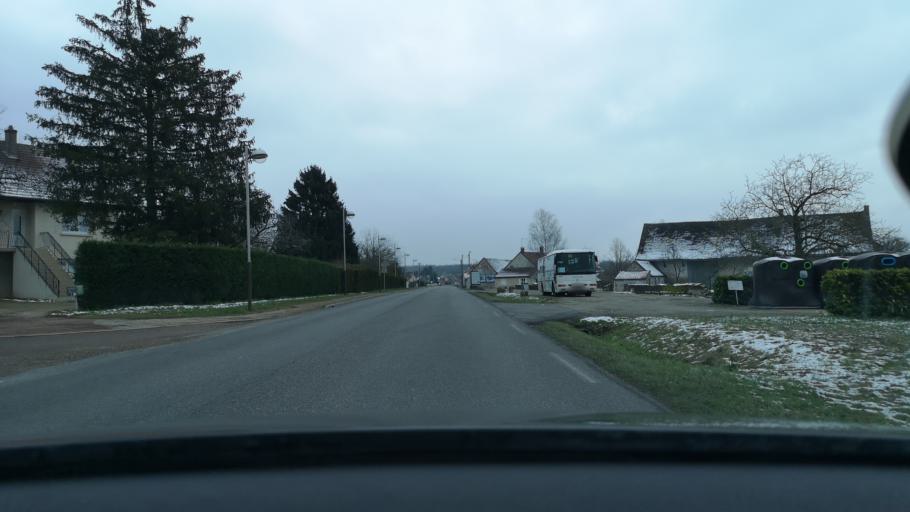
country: FR
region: Bourgogne
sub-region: Departement de Saone-et-Loire
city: Saint-Marcel
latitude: 46.7837
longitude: 4.9250
